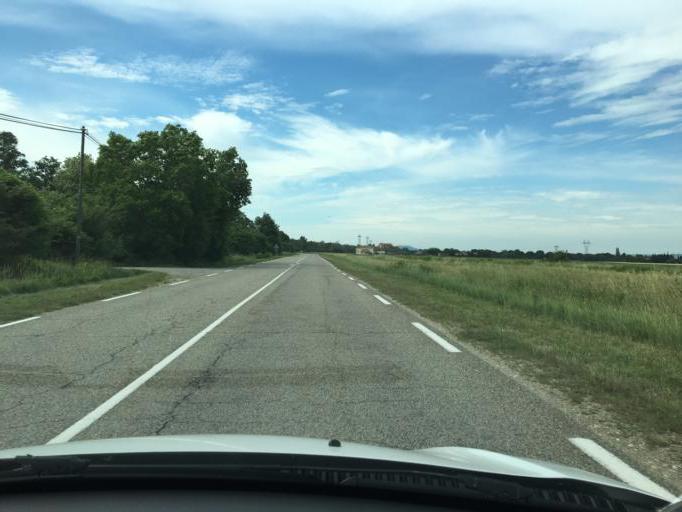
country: FR
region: Provence-Alpes-Cote d'Azur
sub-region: Departement du Vaucluse
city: Bollene
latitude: 44.2999
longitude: 4.7352
